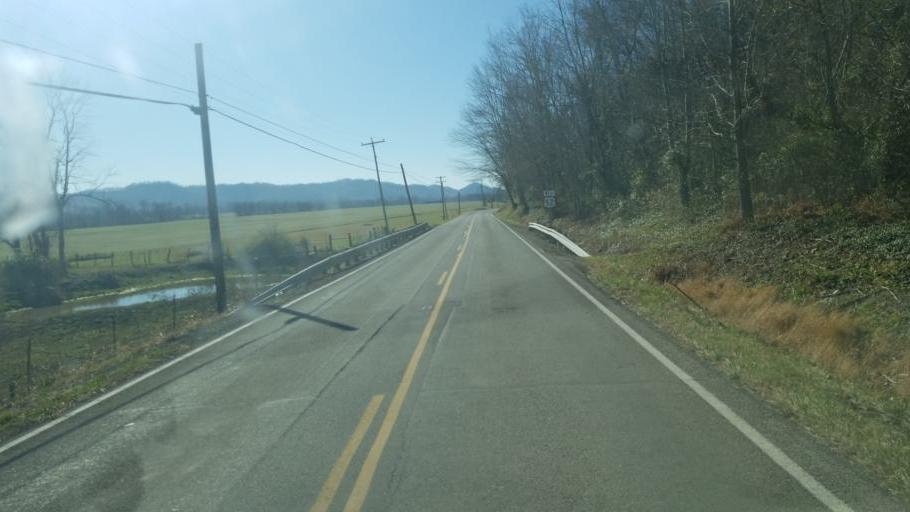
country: US
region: Ohio
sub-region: Scioto County
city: West Portsmouth
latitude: 38.6392
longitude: -83.1439
